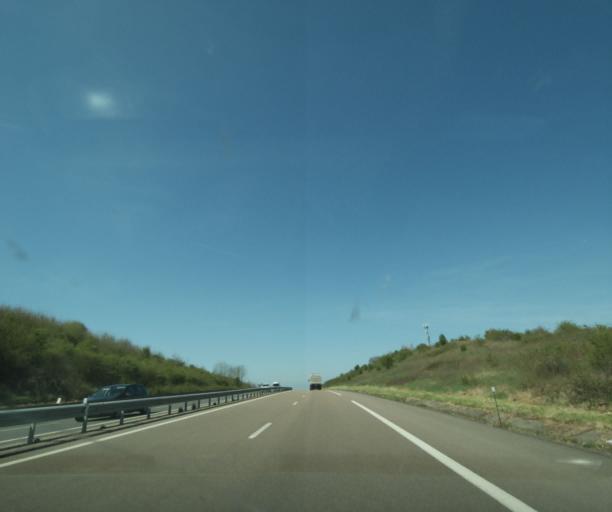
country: FR
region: Bourgogne
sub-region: Departement de la Nievre
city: Pougues-les-Eaux
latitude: 47.0824
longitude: 3.1187
